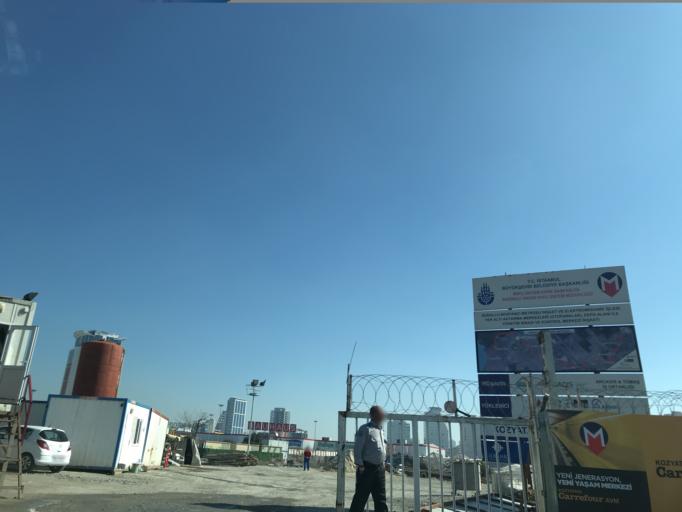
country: TR
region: Istanbul
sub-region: Atasehir
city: Atasehir
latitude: 40.9771
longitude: 29.0987
